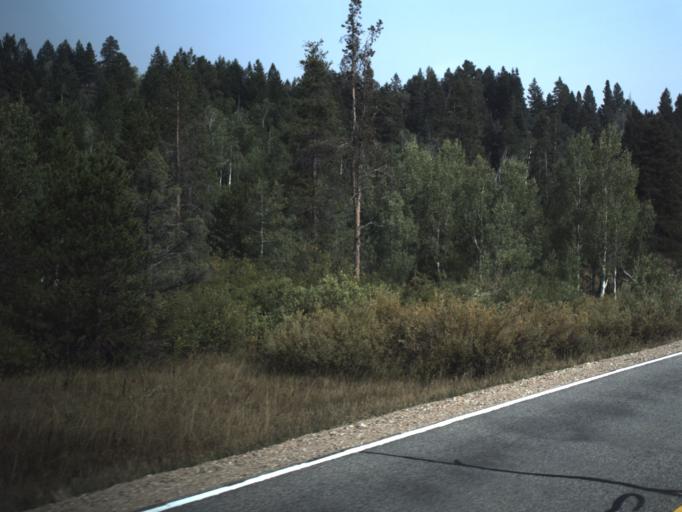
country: US
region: Utah
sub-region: Summit County
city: Francis
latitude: 40.6207
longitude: -111.1357
